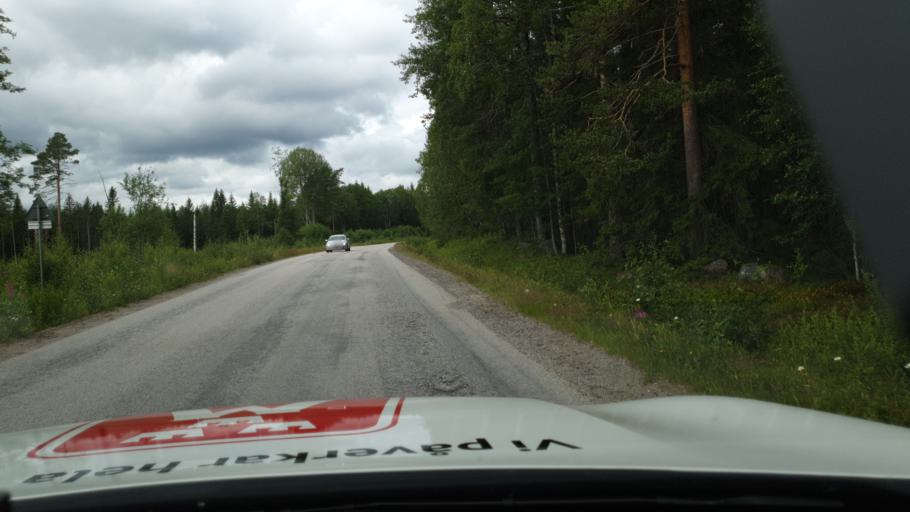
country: SE
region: Vaesterbotten
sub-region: Nordmalings Kommun
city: Nordmaling
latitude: 63.5827
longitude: 19.4627
